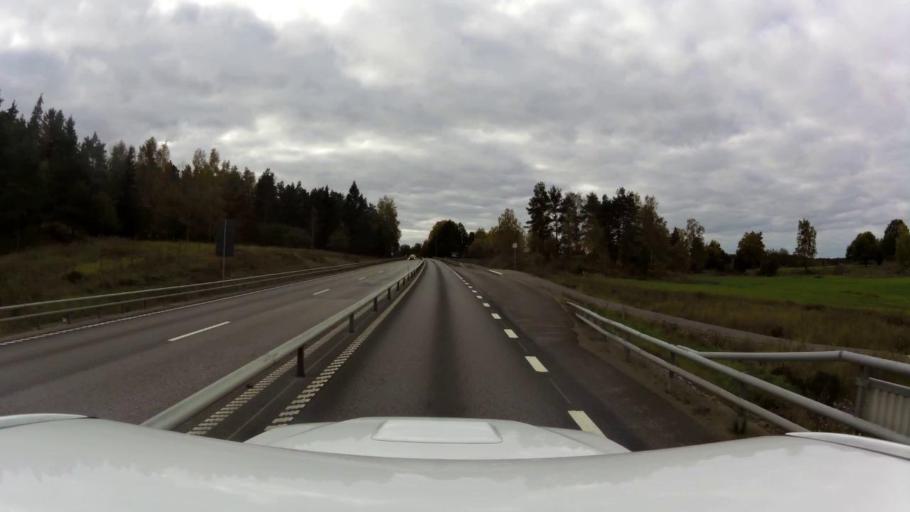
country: SE
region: OEstergoetland
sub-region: Linkopings Kommun
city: Malmslatt
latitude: 58.3049
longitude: 15.5646
